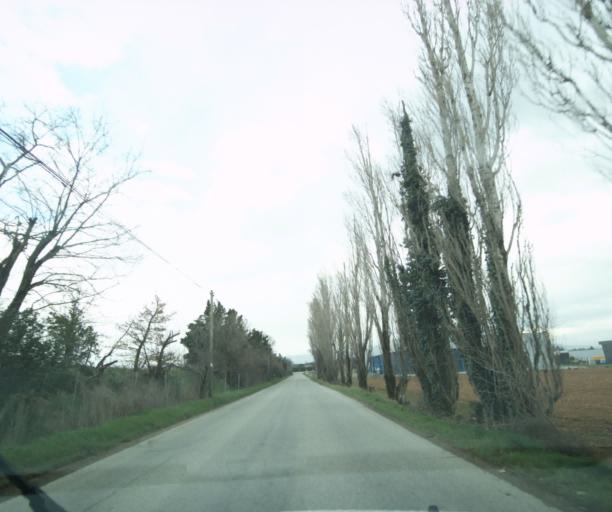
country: FR
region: Rhone-Alpes
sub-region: Departement de la Drome
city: Bourg-les-Valence
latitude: 44.9755
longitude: 4.8927
